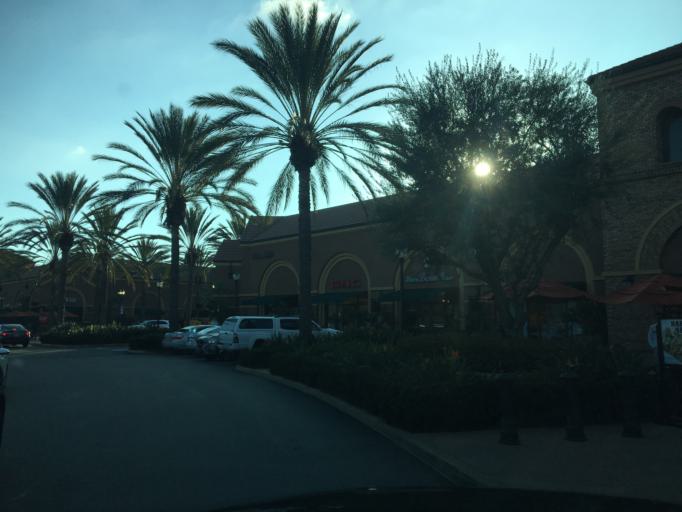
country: US
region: California
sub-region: Orange County
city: Lake Forest
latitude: 33.6983
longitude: -117.7430
